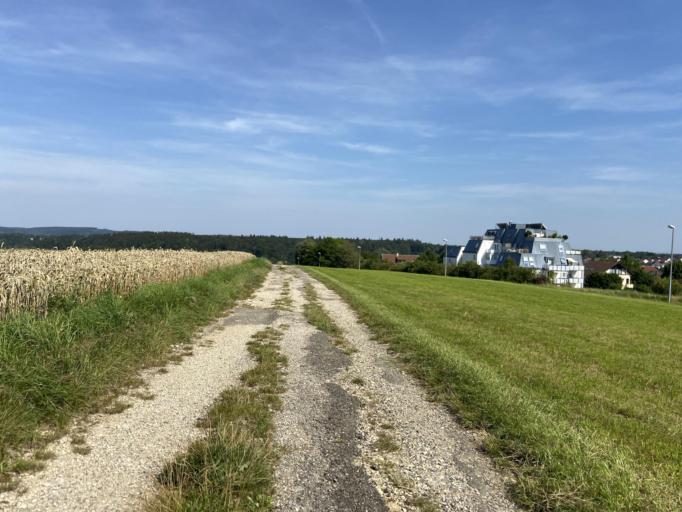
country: DE
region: Baden-Wuerttemberg
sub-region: Tuebingen Region
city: Sigmaringen
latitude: 48.0987
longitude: 9.2283
